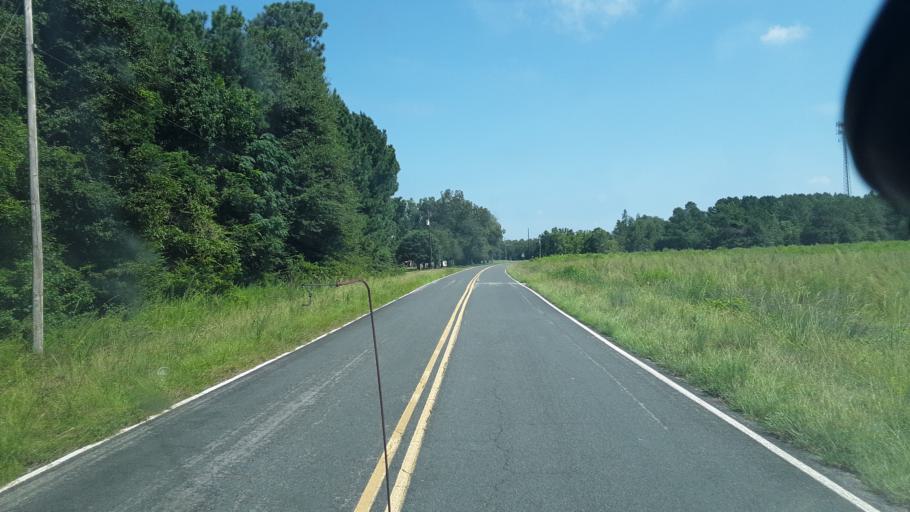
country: US
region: South Carolina
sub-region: Bamberg County
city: Bamberg
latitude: 33.3731
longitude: -81.0138
